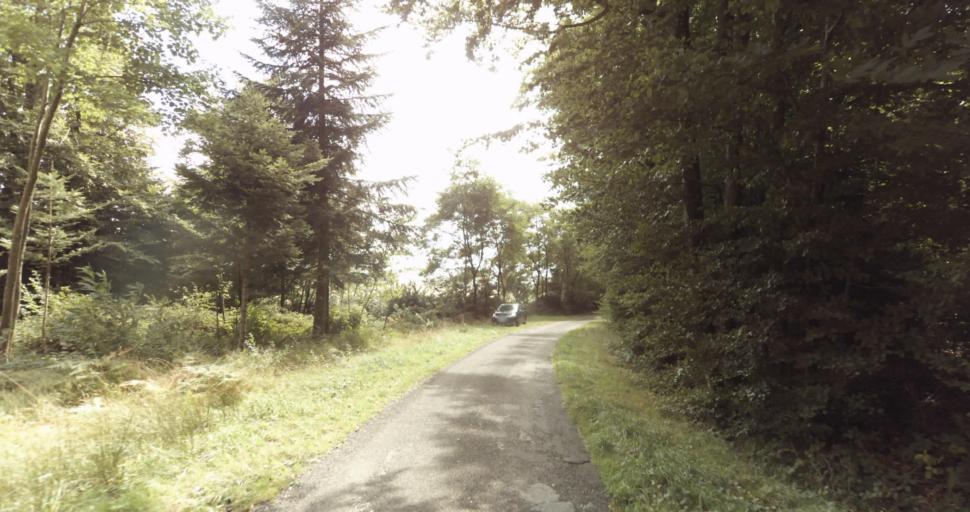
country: FR
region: Lower Normandy
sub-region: Departement de l'Orne
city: Gace
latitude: 48.7818
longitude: 0.3139
